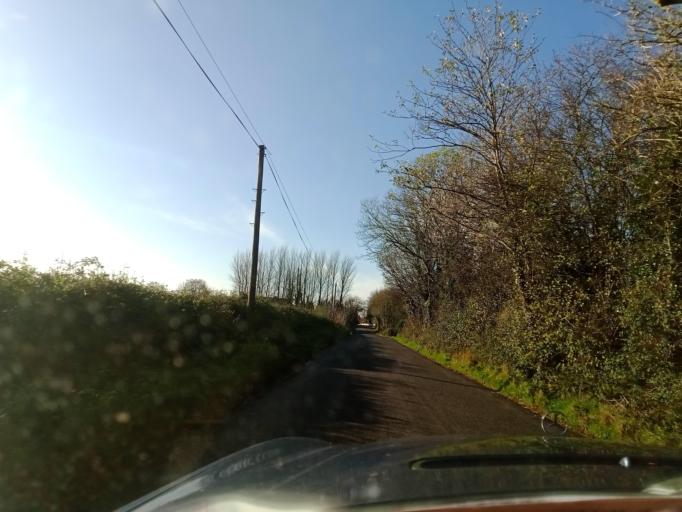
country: IE
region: Leinster
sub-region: Kilkenny
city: Mooncoin
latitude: 52.2959
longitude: -7.2239
